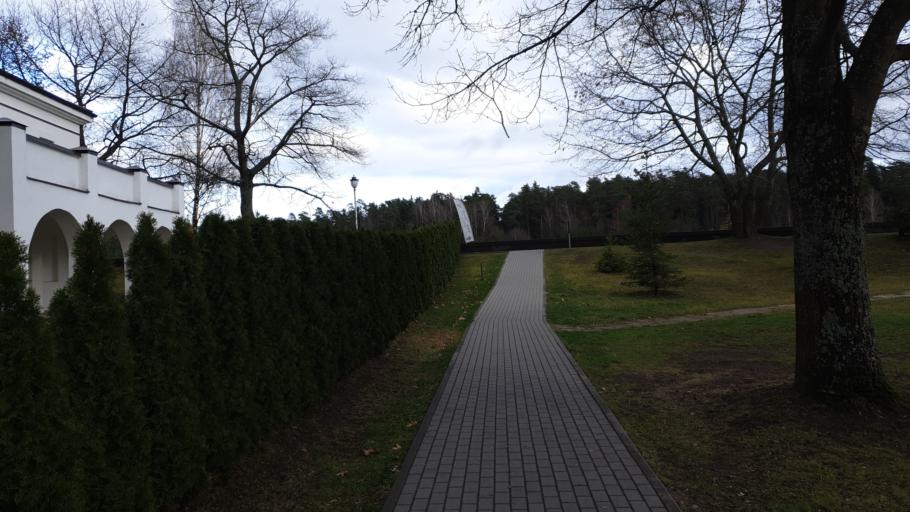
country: LT
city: Birstonas
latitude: 54.6015
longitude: 24.0358
